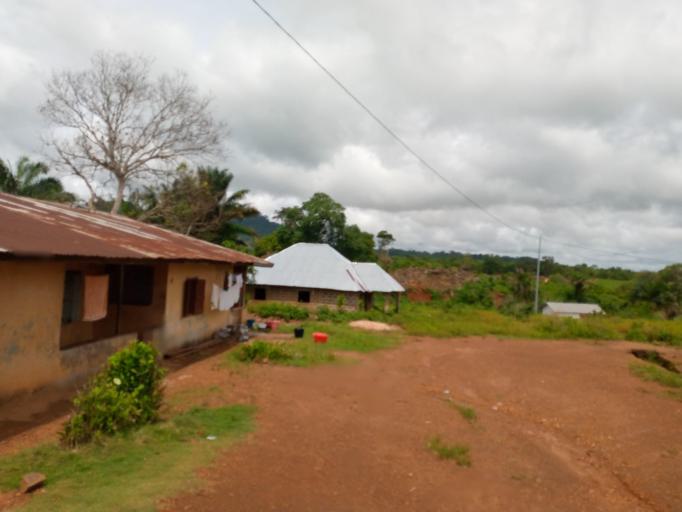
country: SL
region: Southern Province
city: Mogbwemo
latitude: 7.7579
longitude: -12.3101
